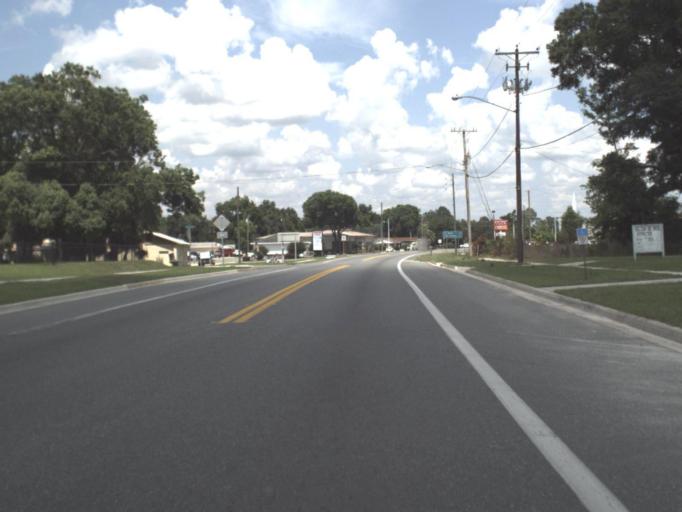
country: US
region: Florida
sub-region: Lafayette County
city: Mayo
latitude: 29.9562
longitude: -82.9261
